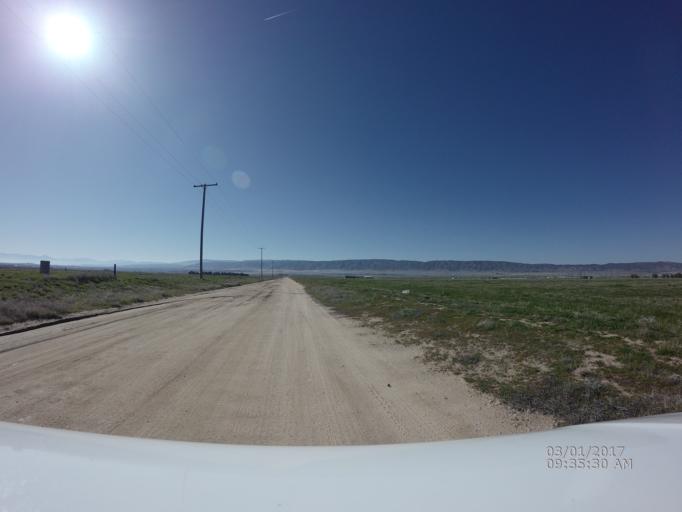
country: US
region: California
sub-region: Los Angeles County
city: Quartz Hill
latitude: 34.7018
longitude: -118.2718
